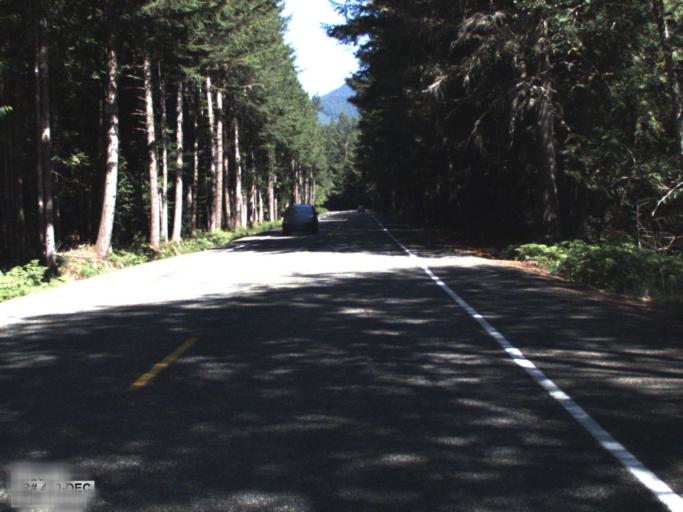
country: US
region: Washington
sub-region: King County
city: Riverbend
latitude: 47.1299
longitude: -121.6176
